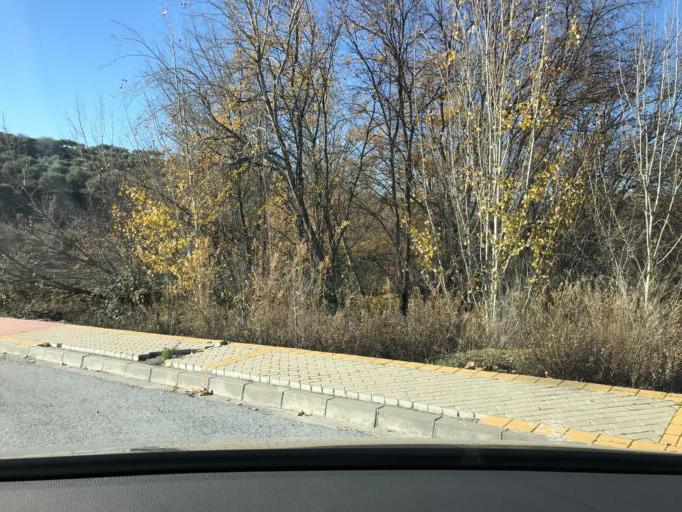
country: ES
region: Andalusia
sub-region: Provincia de Granada
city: Jun
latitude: 37.2193
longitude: -3.5797
